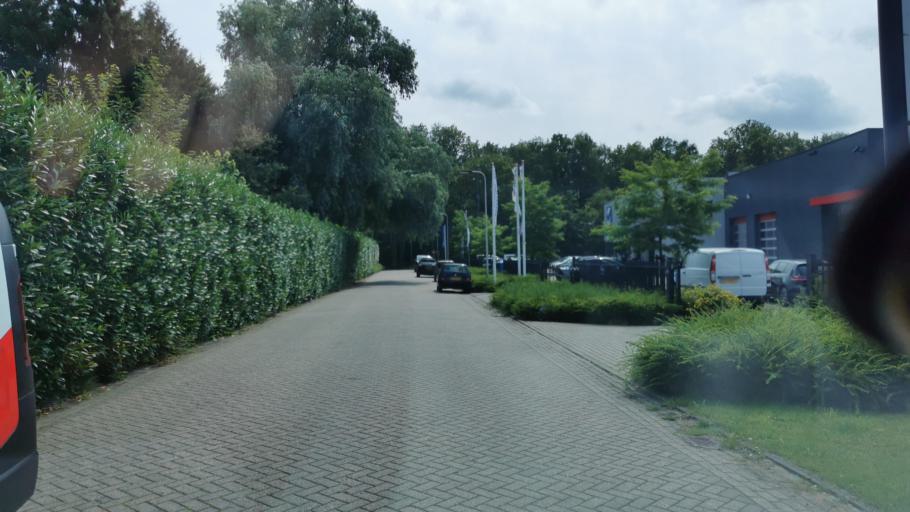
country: NL
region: Overijssel
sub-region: Gemeente Enschede
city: Enschede
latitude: 52.2235
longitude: 6.9420
